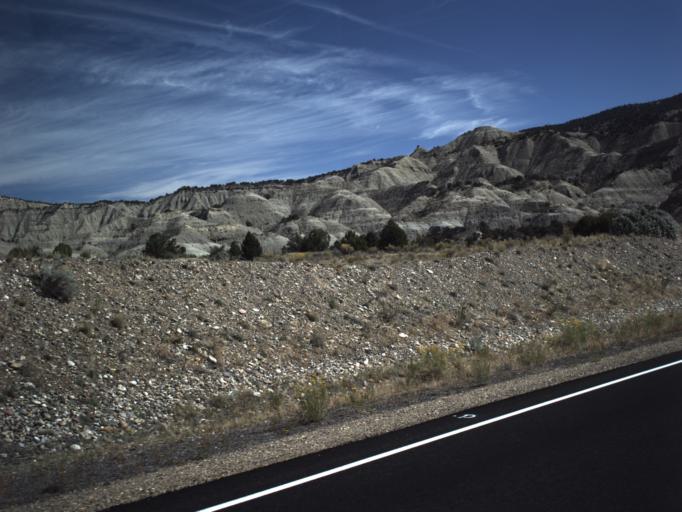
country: US
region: Utah
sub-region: Garfield County
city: Panguitch
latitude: 37.6217
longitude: -111.8673
